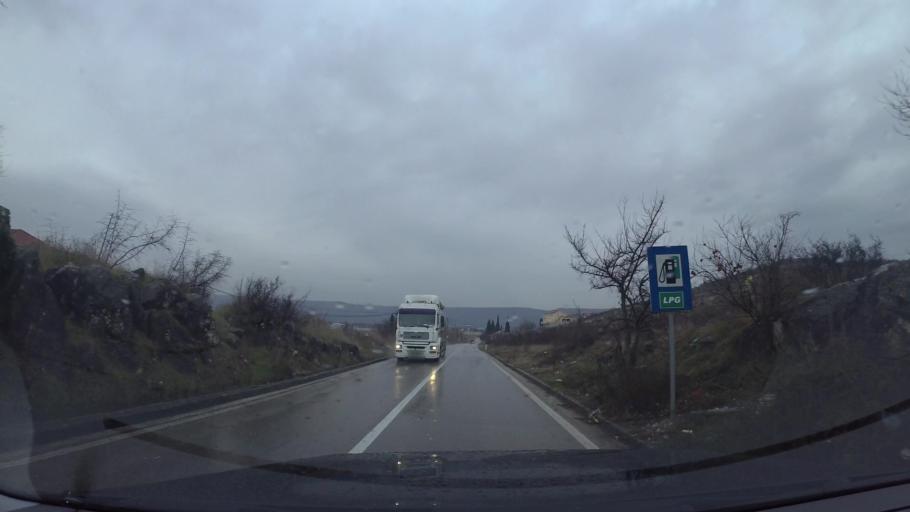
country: BA
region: Federation of Bosnia and Herzegovina
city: Blagaj
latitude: 43.2900
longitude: 17.8542
